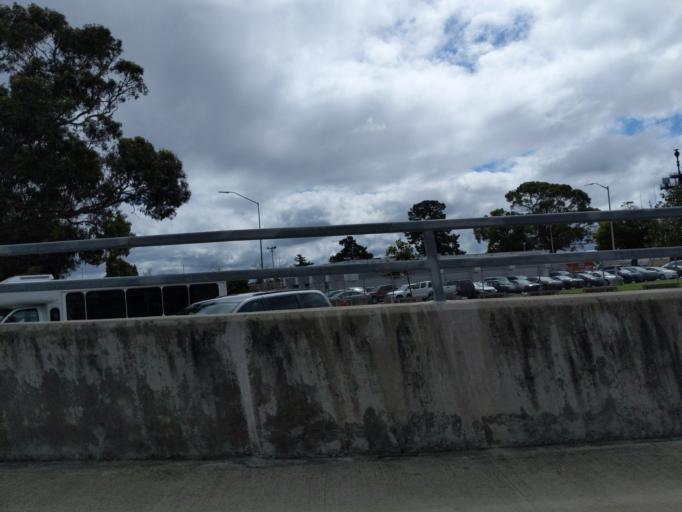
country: US
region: California
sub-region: Alameda County
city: Alameda
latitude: 37.7801
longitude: -122.2463
